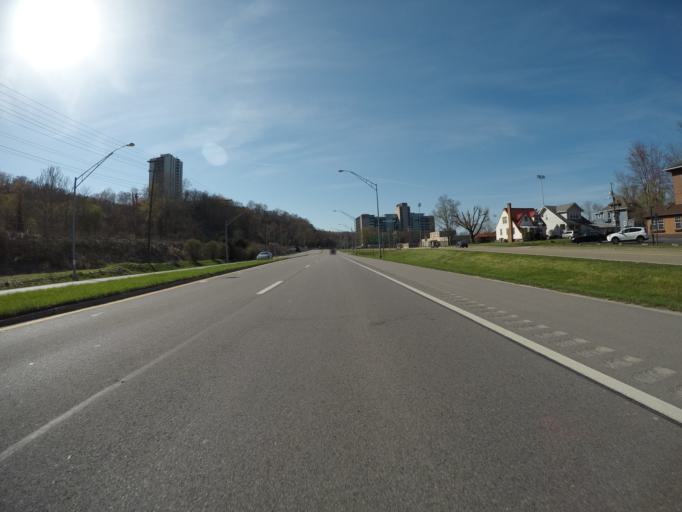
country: US
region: West Virginia
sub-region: Kanawha County
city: Charleston
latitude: 38.3334
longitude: -81.6206
